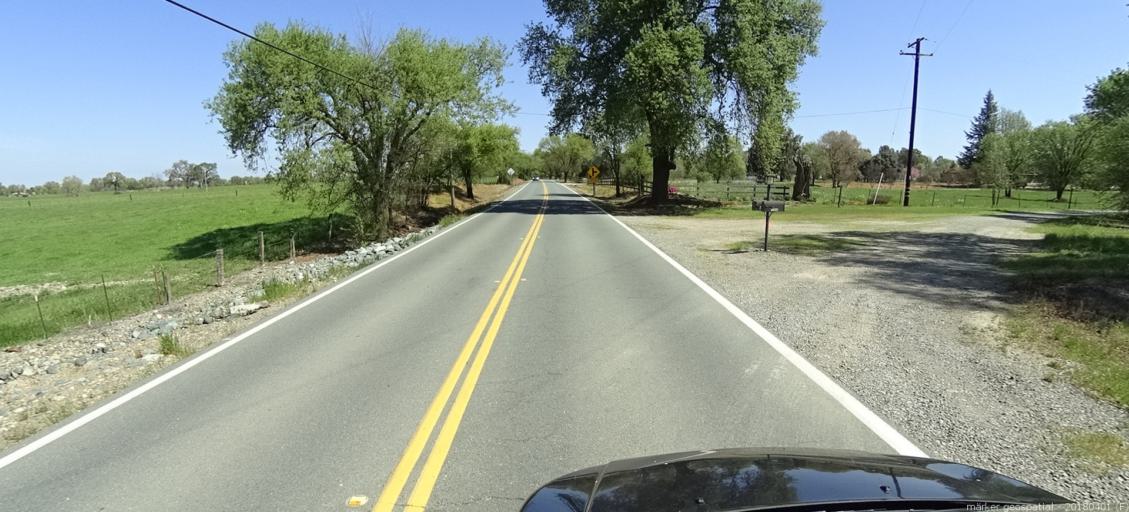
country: US
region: California
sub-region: Sacramento County
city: Wilton
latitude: 38.4136
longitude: -121.2570
